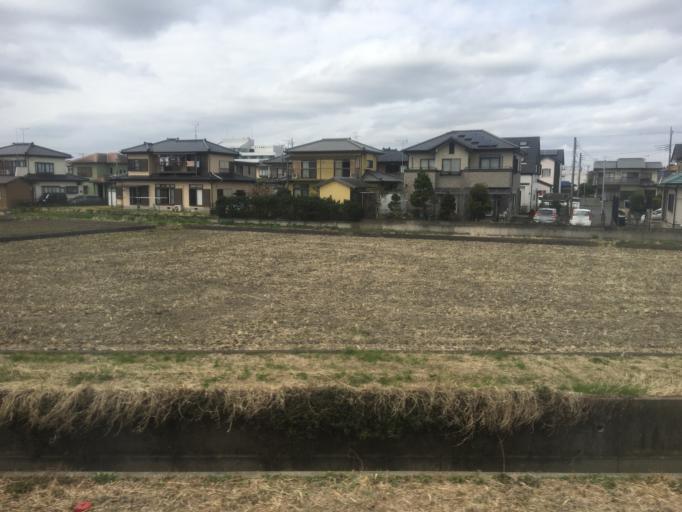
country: JP
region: Chiba
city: Naruto
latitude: 35.5999
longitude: 140.4152
